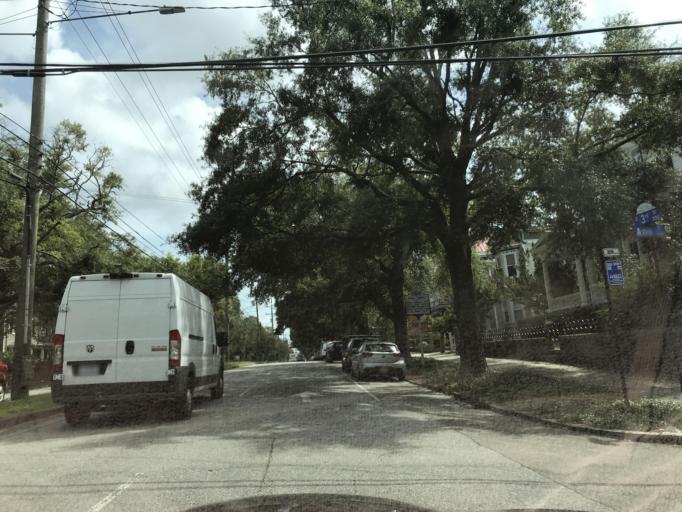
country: US
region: North Carolina
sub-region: New Hanover County
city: Wilmington
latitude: 34.2321
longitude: -77.9457
